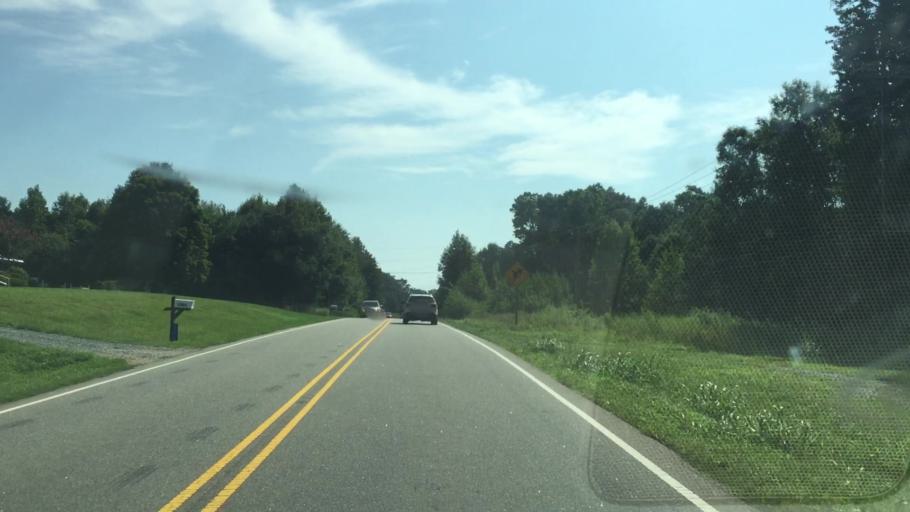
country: US
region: North Carolina
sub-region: Union County
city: Unionville
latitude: 35.1323
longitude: -80.4676
